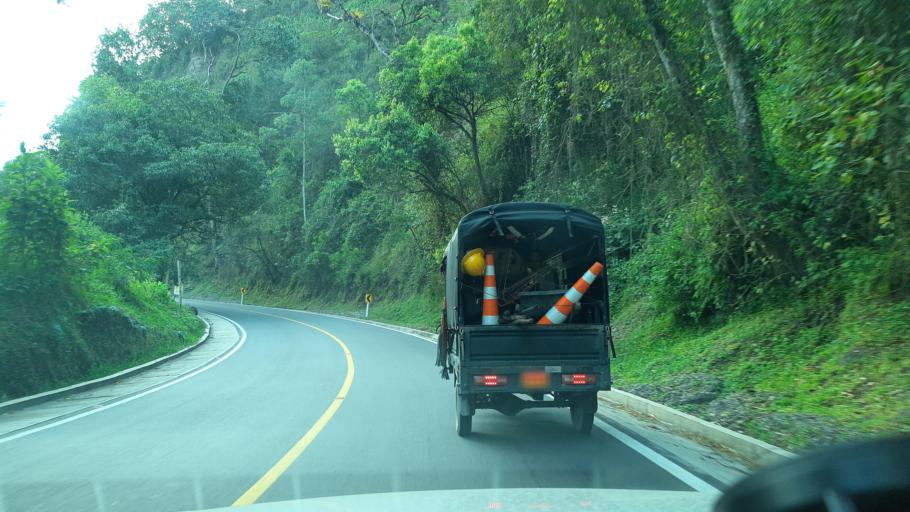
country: CO
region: Boyaca
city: Somondoco
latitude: 4.9832
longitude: -73.3439
